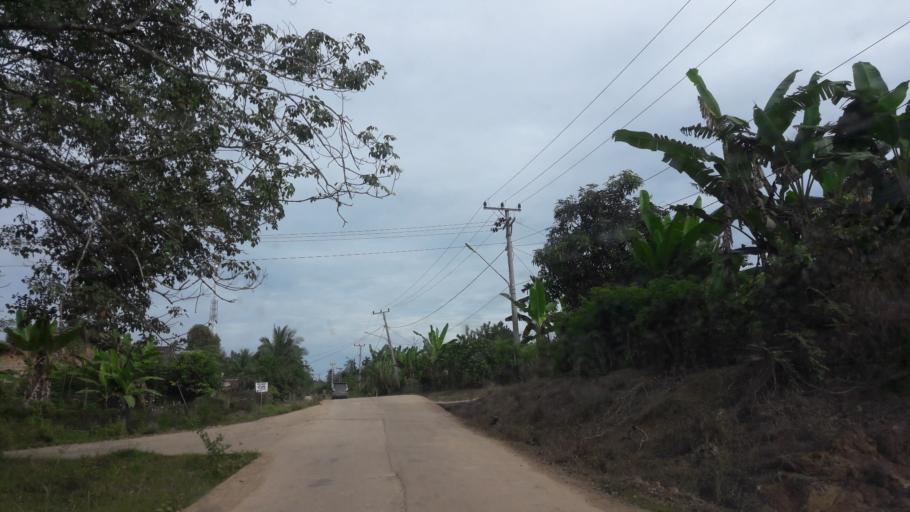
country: ID
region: South Sumatra
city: Gunungmegang Dalam
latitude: -3.2920
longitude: 103.6779
